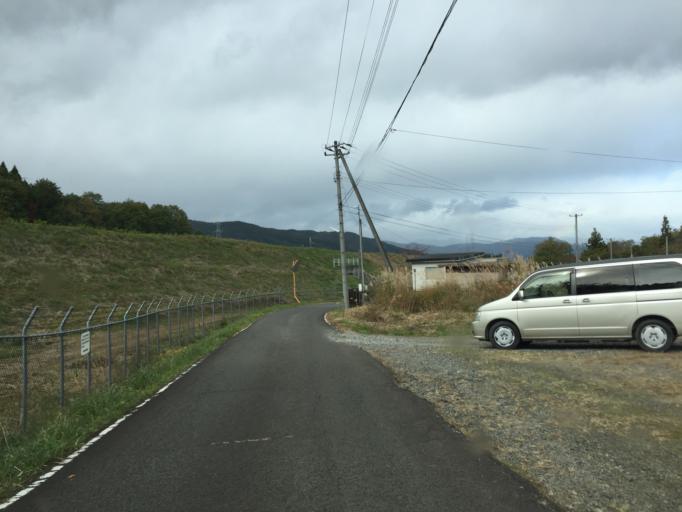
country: JP
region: Fukushima
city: Fukushima-shi
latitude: 37.6985
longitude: 140.3591
